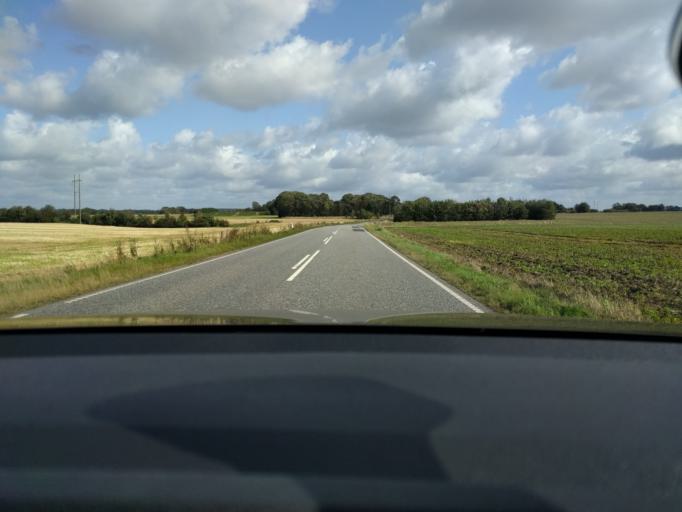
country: DK
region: Central Jutland
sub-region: Viborg Kommune
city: Bjerringbro
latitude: 56.3077
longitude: 9.7268
